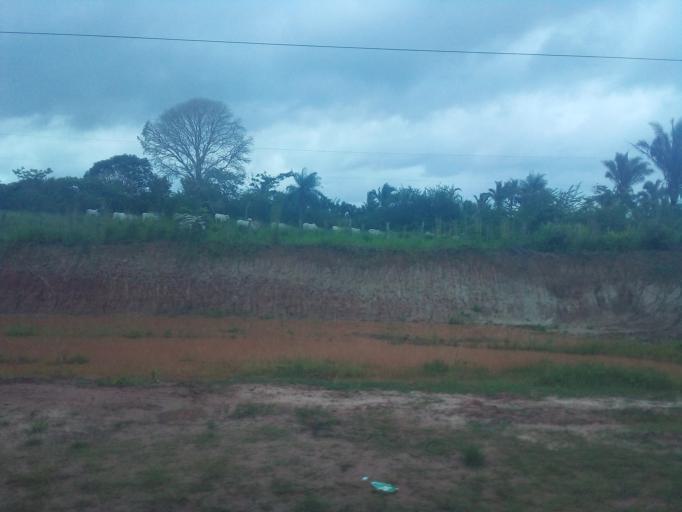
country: BR
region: Maranhao
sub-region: Arari
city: Arari
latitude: -3.5752
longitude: -44.7043
